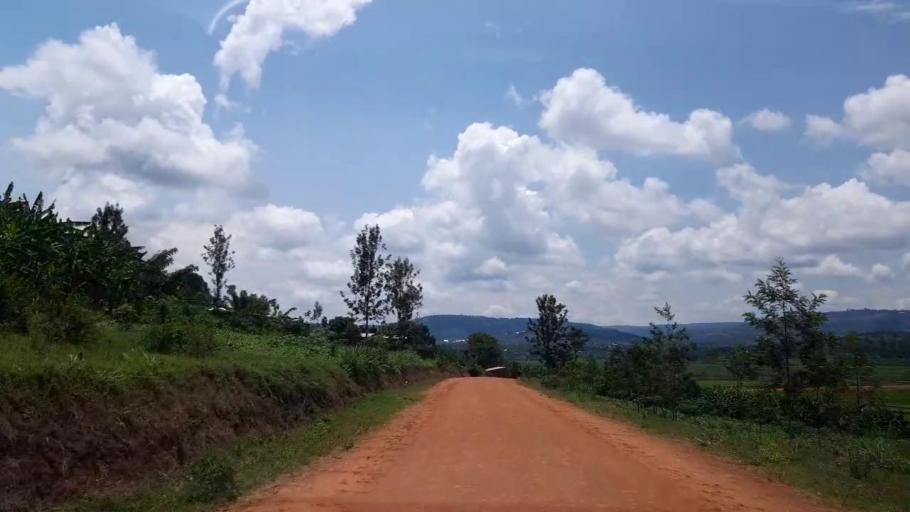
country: RW
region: Northern Province
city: Byumba
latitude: -1.5695
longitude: 30.2954
